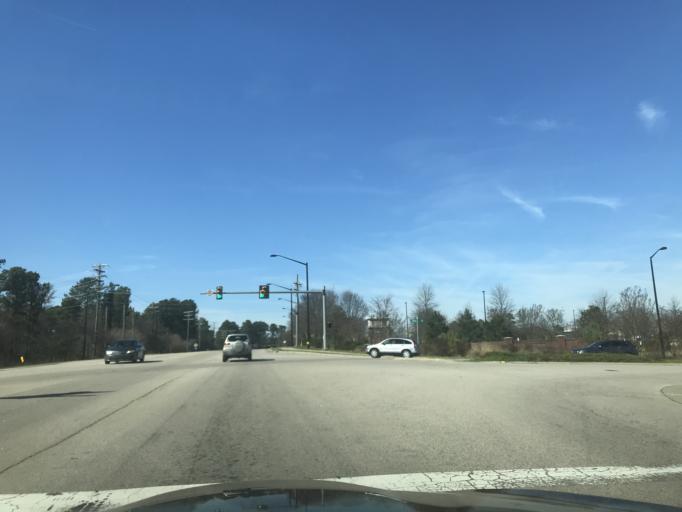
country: US
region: North Carolina
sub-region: Wake County
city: Morrisville
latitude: 35.8654
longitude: -78.8480
